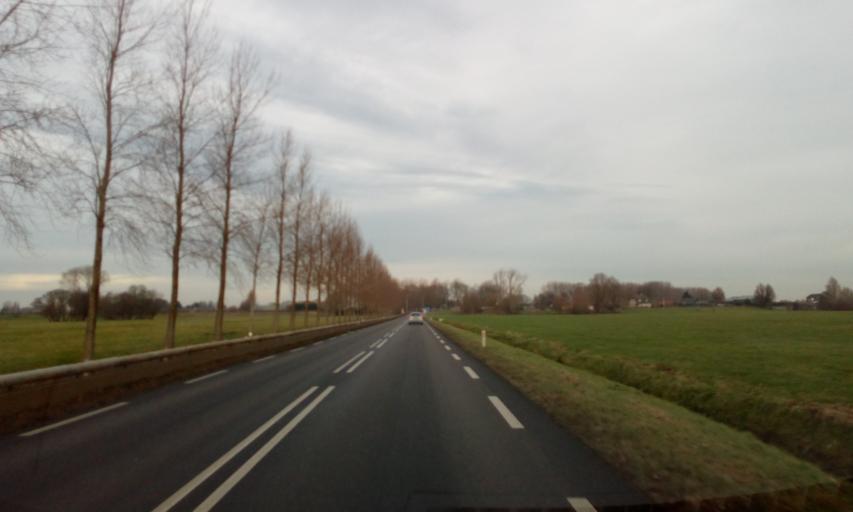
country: NL
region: South Holland
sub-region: Gemeente Zoetermeer
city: Zoetermeer
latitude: 52.0869
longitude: 4.4740
